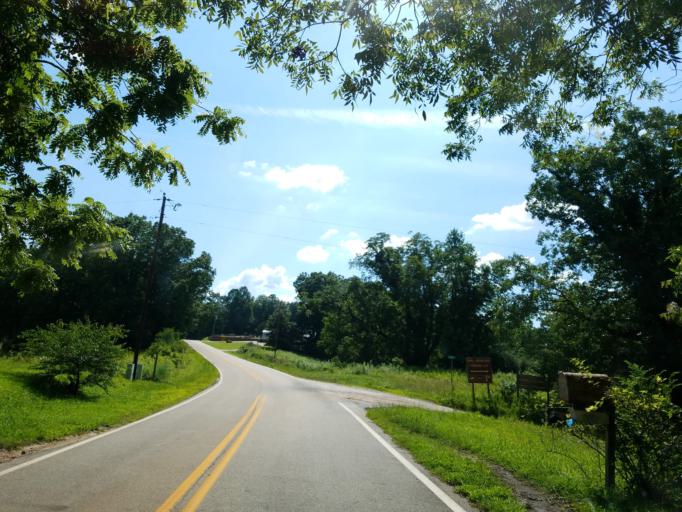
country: US
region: Georgia
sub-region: Dawson County
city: Dawsonville
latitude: 34.5644
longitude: -84.1380
